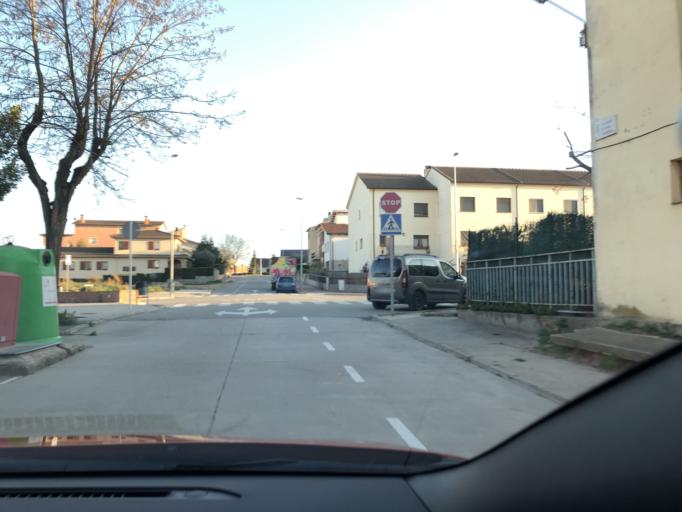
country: ES
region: Catalonia
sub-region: Provincia de Lleida
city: Solsona
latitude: 41.9902
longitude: 1.5150
